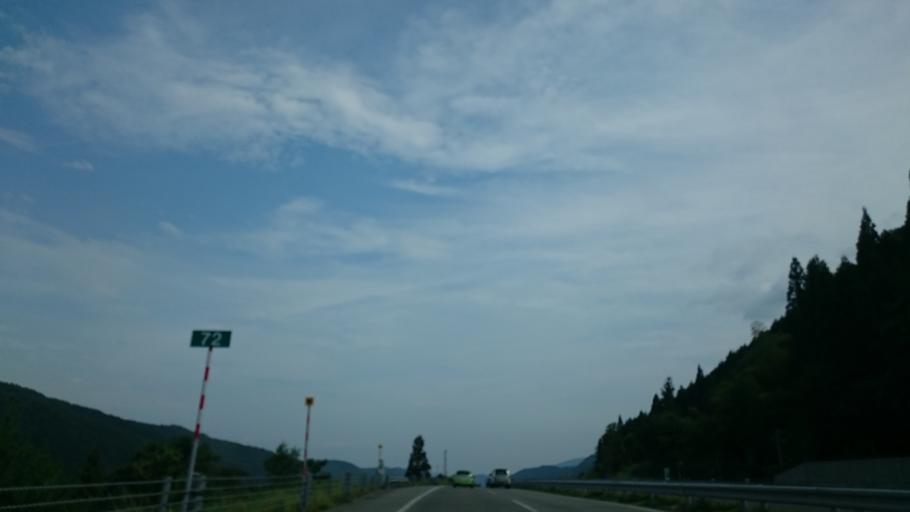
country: JP
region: Gifu
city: Gujo
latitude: 35.8380
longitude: 136.8783
